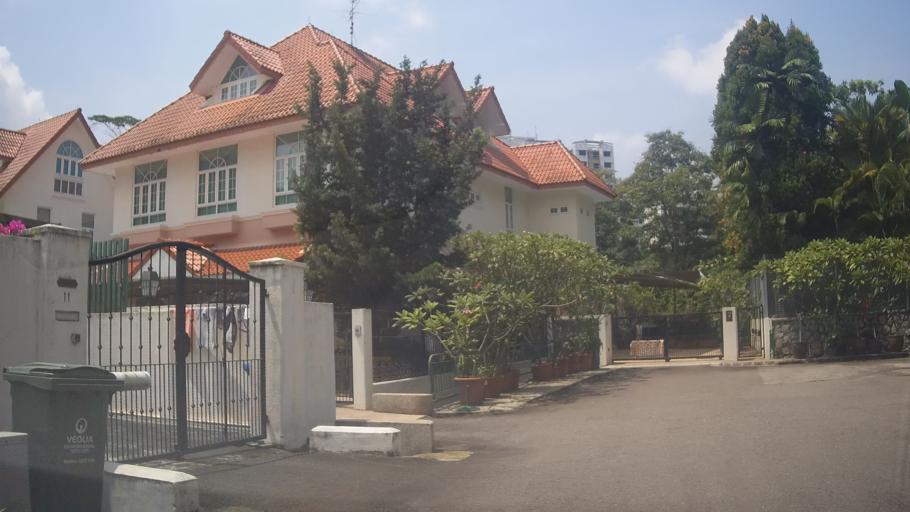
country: SG
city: Singapore
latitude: 1.3148
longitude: 103.7881
